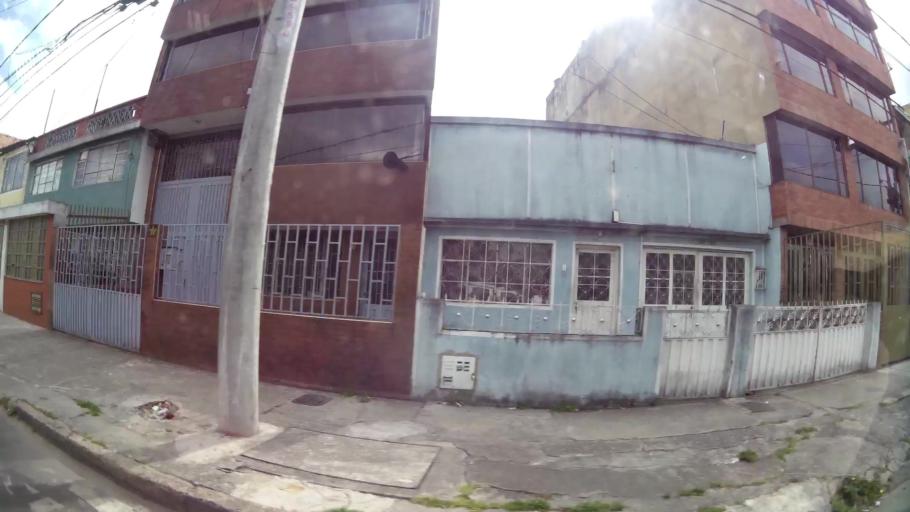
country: CO
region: Bogota D.C.
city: Bogota
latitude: 4.6157
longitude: -74.1061
